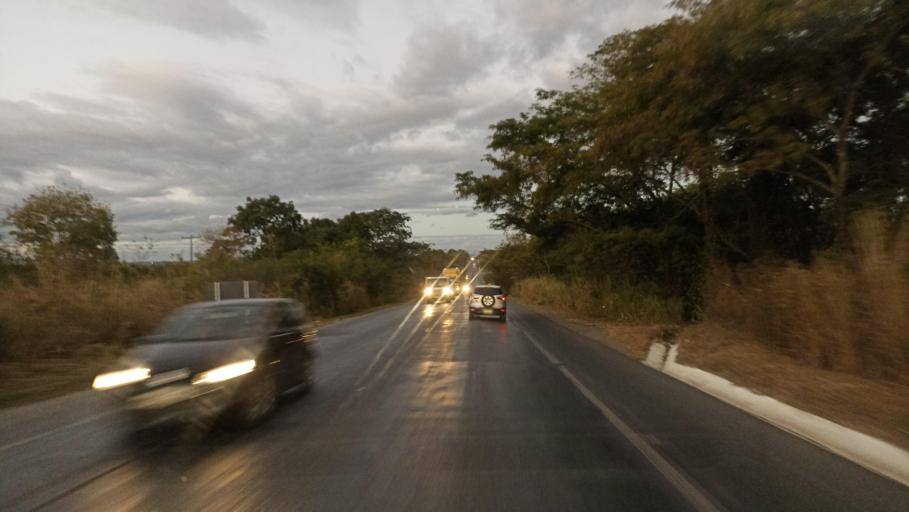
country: BR
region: Minas Gerais
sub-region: Montes Claros
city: Montes Claros
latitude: -16.6584
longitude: -43.7338
